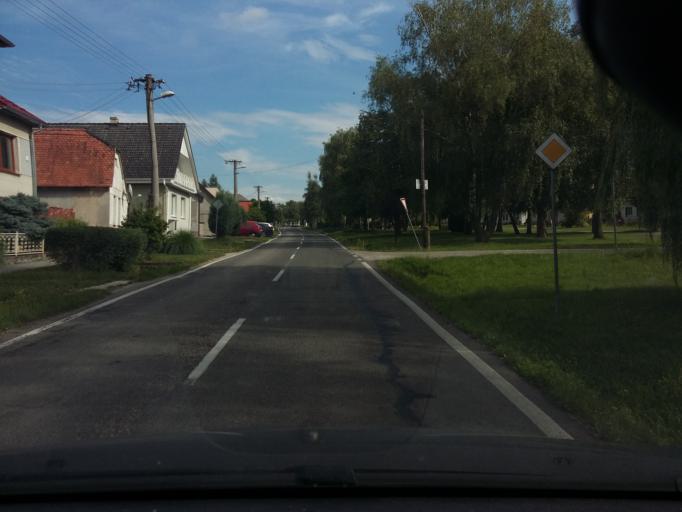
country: SK
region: Trnavsky
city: Gbely
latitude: 48.5805
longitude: 17.1813
